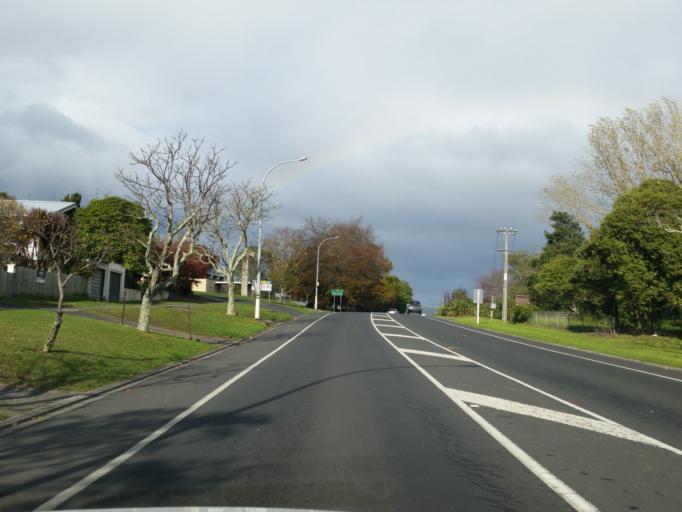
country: NZ
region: Waikato
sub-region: Hauraki District
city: Paeroa
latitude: -37.3851
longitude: 175.6777
